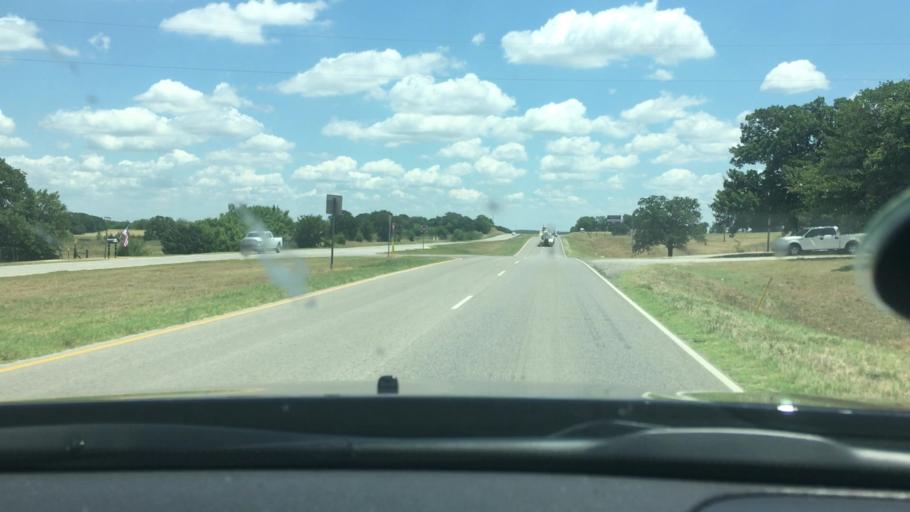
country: US
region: Oklahoma
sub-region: Carter County
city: Wilson
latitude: 34.1728
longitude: -97.3944
